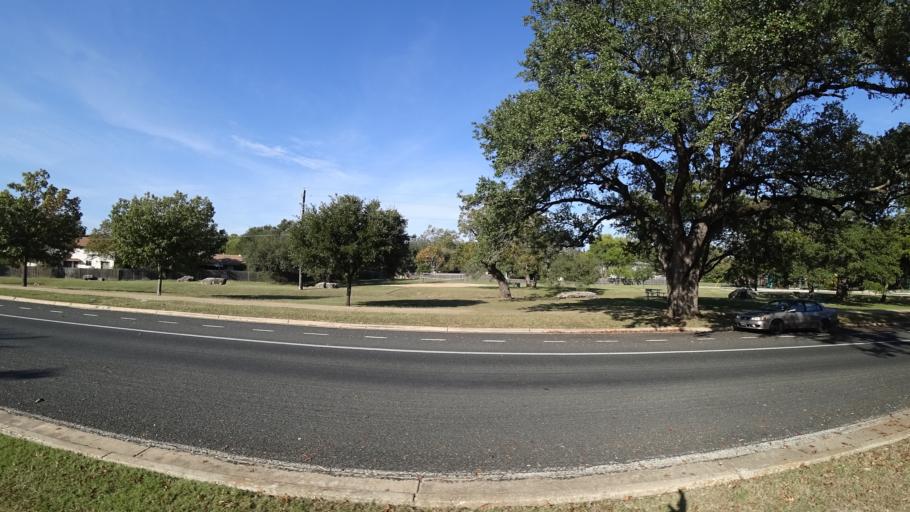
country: US
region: Texas
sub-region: Williamson County
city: Anderson Mill
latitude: 30.4587
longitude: -97.8120
